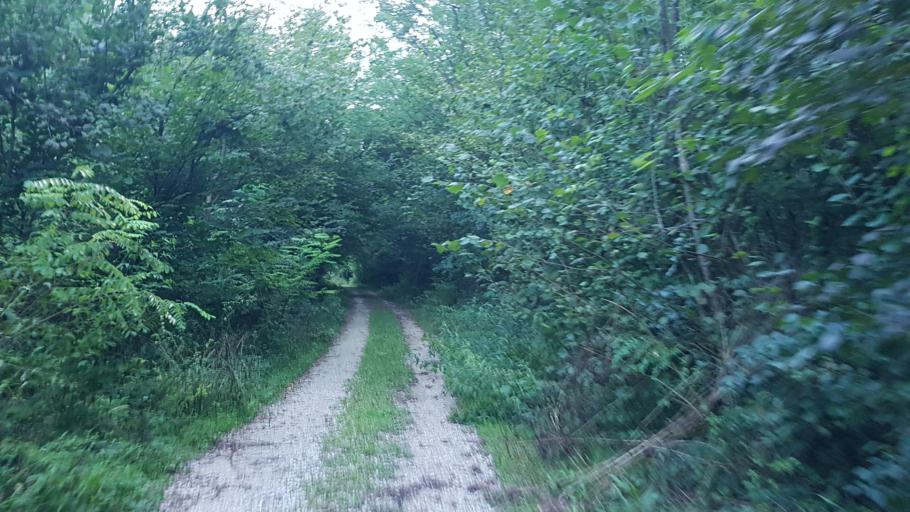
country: IT
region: Friuli Venezia Giulia
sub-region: Provincia di Gorizia
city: San Lorenzo Isontino
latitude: 45.9458
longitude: 13.5329
